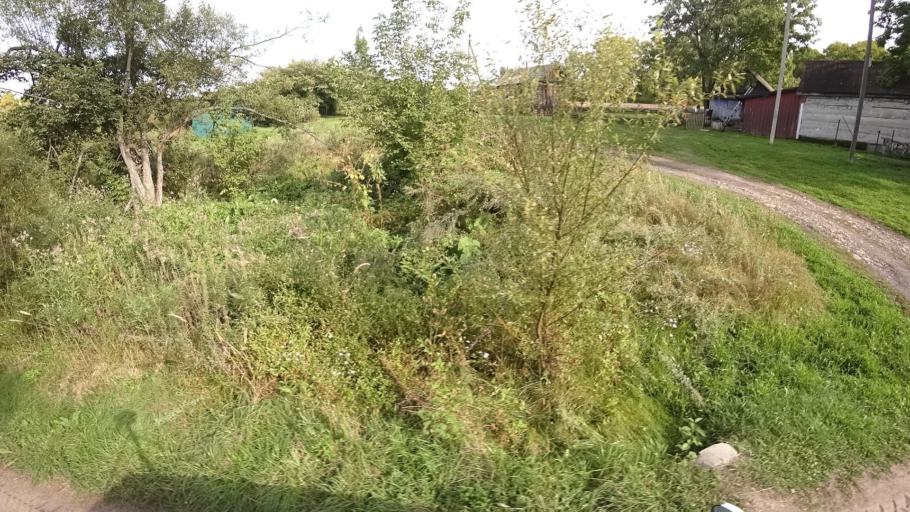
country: RU
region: Primorskiy
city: Dostoyevka
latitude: 44.2937
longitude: 133.4523
